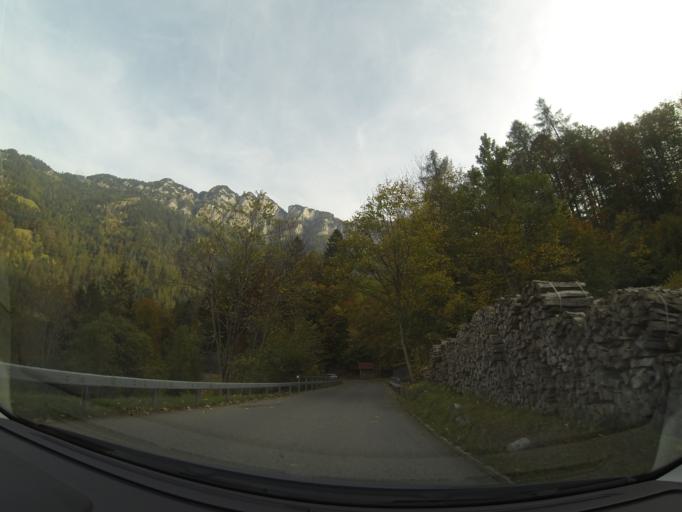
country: CH
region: Grisons
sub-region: Landquart District
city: Untervaz
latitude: 46.9496
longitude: 9.4770
